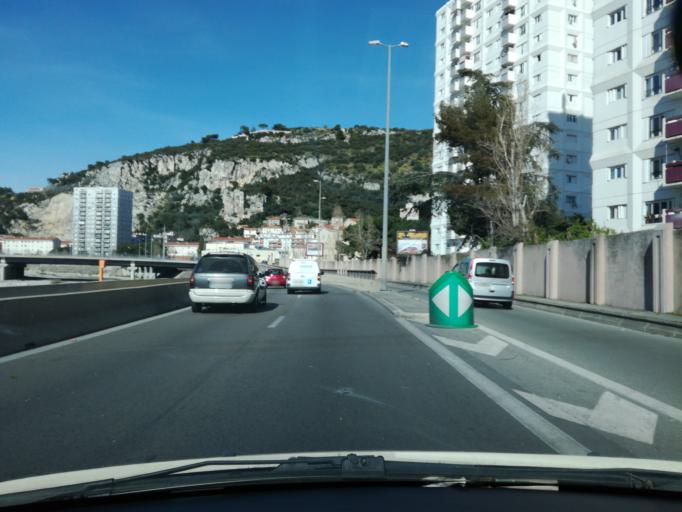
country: FR
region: Provence-Alpes-Cote d'Azur
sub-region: Departement des Alpes-Maritimes
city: Saint-Andre-de-la-Roche
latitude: 43.7214
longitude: 7.2880
